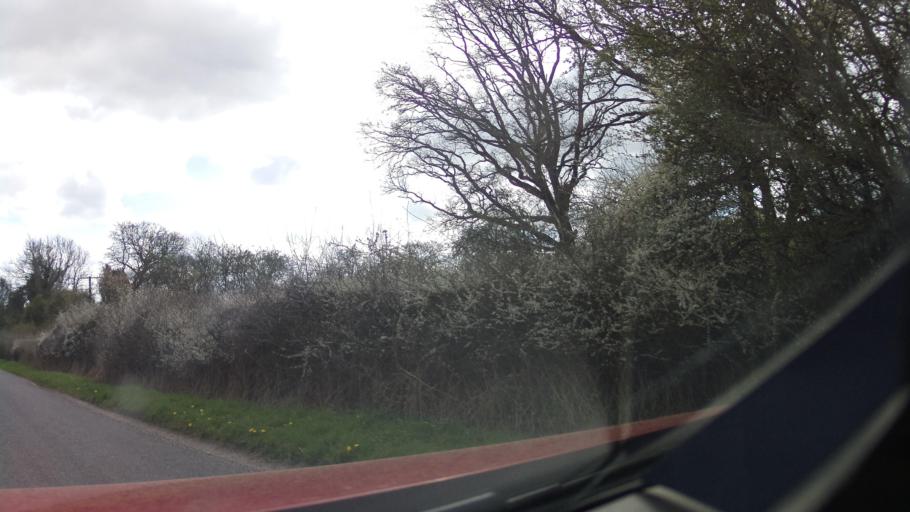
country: GB
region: England
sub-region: Hampshire
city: Highclere
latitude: 51.2922
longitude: -1.4443
